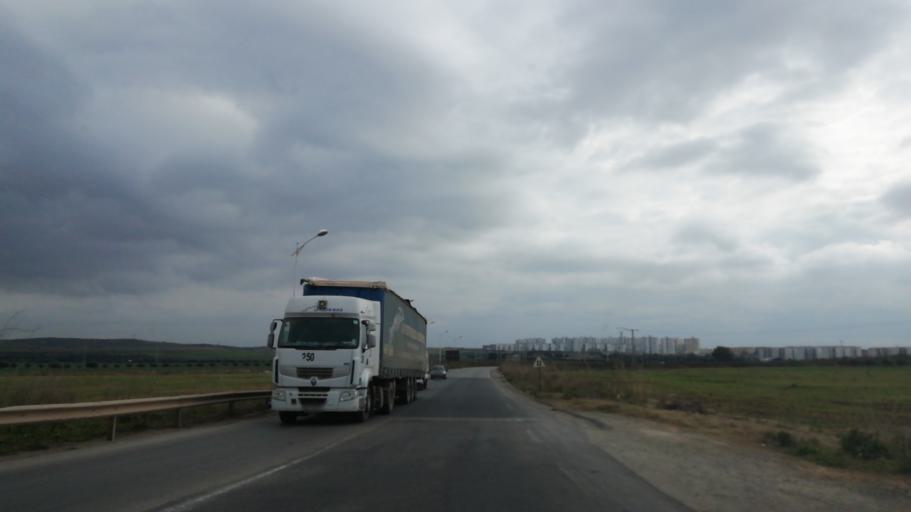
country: DZ
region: Oran
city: Sidi ech Chahmi
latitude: 35.5671
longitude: -0.4495
